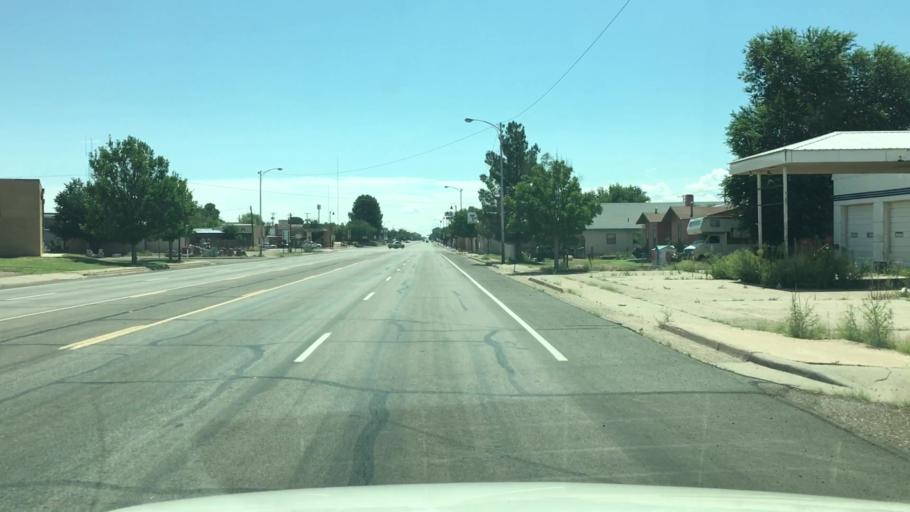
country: US
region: New Mexico
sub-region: De Baca County
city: Fort Sumner
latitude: 34.4724
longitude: -104.2476
